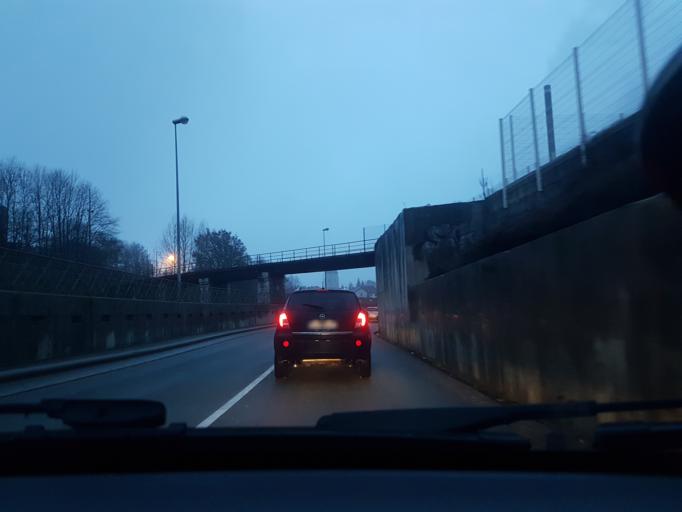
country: FR
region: Franche-Comte
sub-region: Departement du Doubs
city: Pontarlier
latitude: 46.8977
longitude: 6.3598
